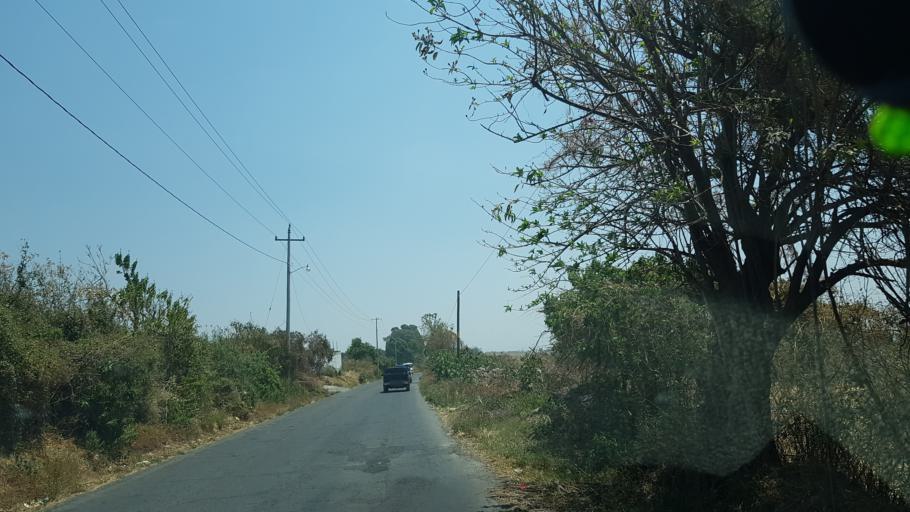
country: MX
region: Puebla
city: Tochimilco
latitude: 18.8866
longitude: -98.5514
